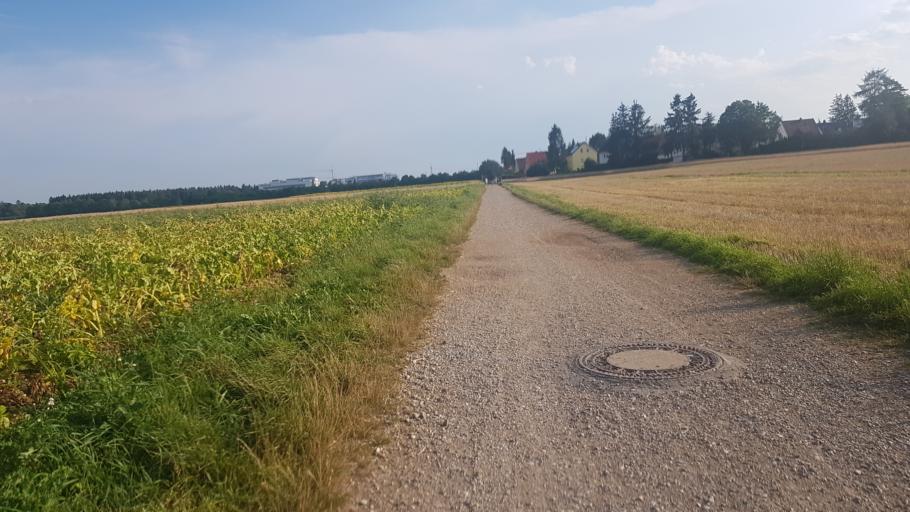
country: DE
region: Bavaria
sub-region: Upper Bavaria
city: Pasing
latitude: 48.1318
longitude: 11.4542
